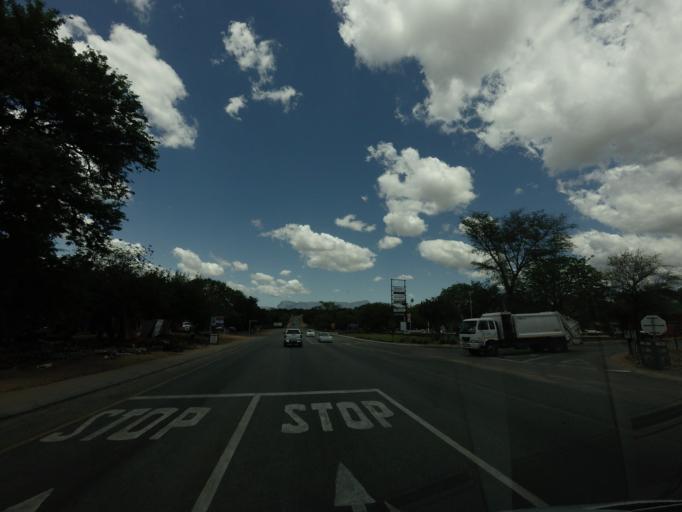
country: ZA
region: Limpopo
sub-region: Mopani District Municipality
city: Hoedspruit
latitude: -24.3559
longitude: 30.9483
